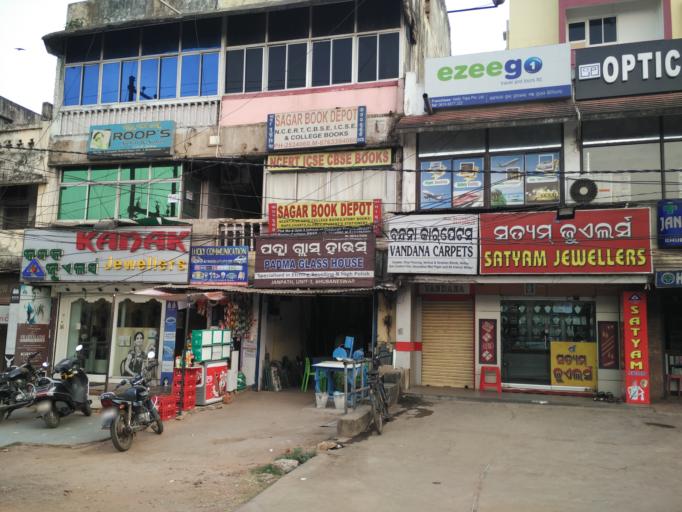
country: IN
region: Odisha
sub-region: Khordha
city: Bhubaneshwar
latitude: 20.2717
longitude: 85.8424
